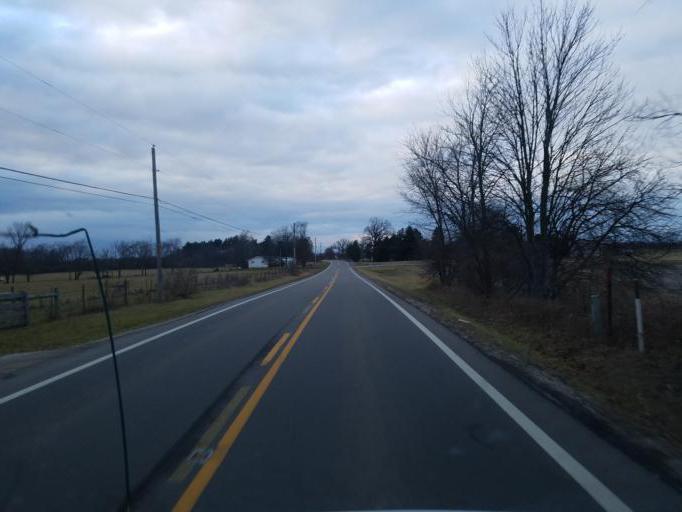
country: US
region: Ohio
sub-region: Delaware County
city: Delaware
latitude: 40.3358
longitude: -83.1326
